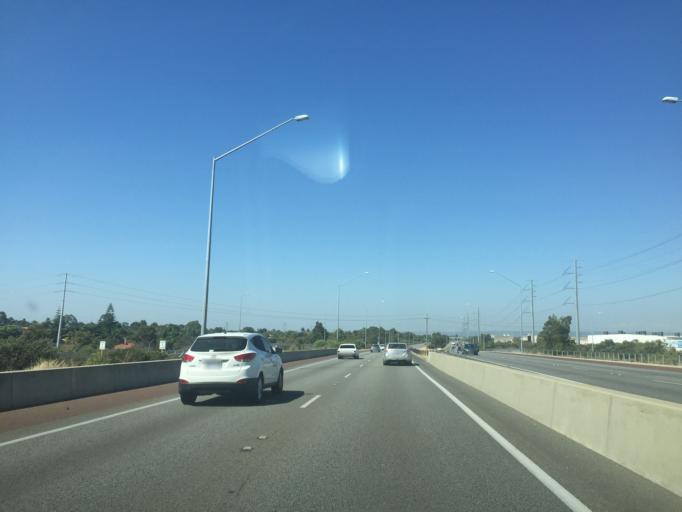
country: AU
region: Western Australia
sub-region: Canning
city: Willetton
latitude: -32.0683
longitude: 115.8907
